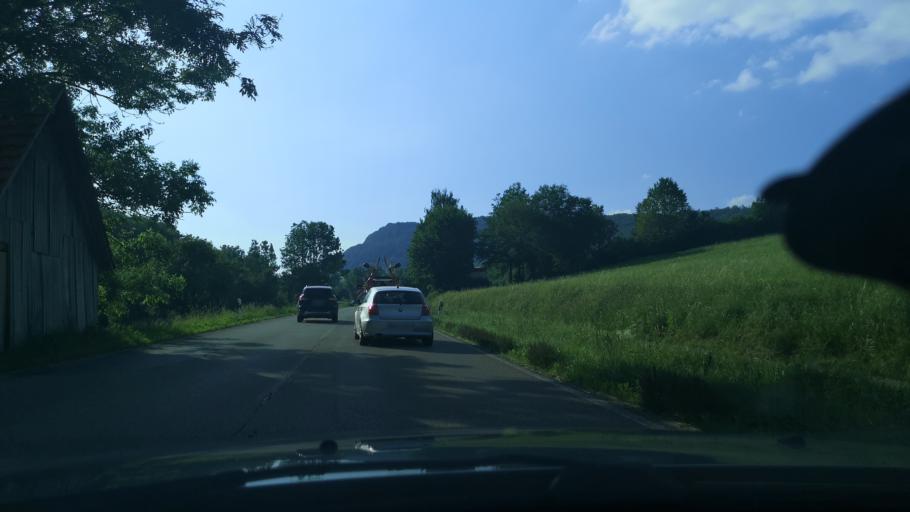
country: DE
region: Baden-Wuerttemberg
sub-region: Regierungsbezirk Stuttgart
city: Deggingen
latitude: 48.6216
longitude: 9.7290
